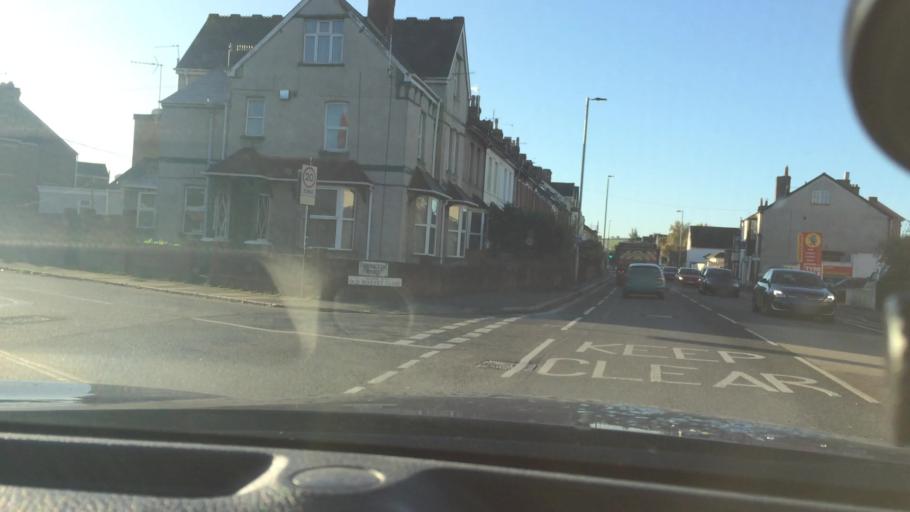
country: GB
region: England
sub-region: Devon
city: Exeter
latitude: 50.7124
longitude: -3.5372
